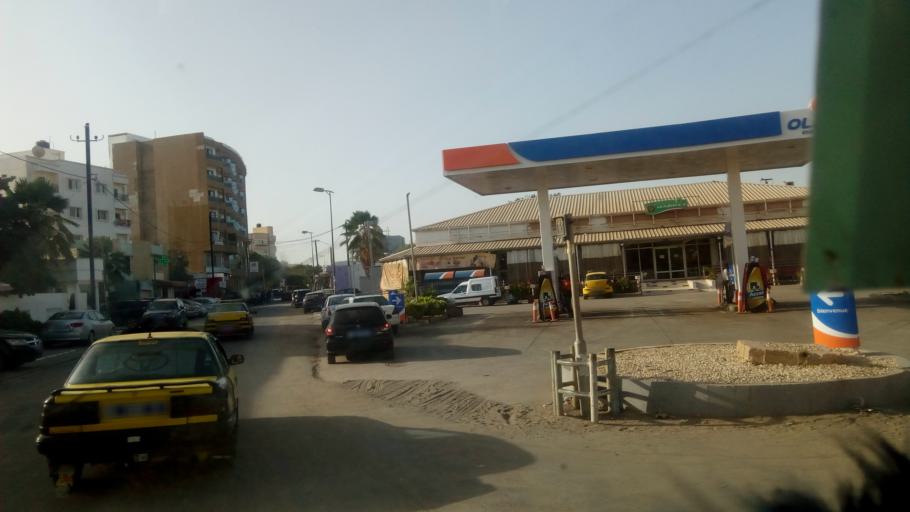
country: SN
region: Dakar
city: Dakar
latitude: 14.7047
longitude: -17.4469
